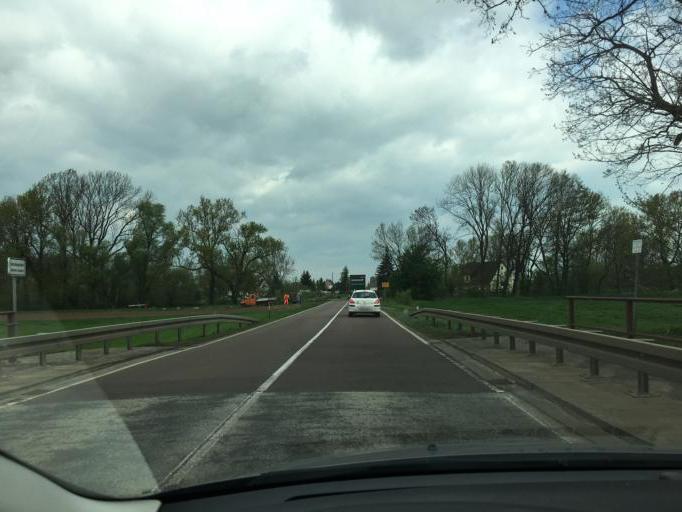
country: DE
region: Saxony-Anhalt
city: Giersleben
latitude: 51.7761
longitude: 11.5852
